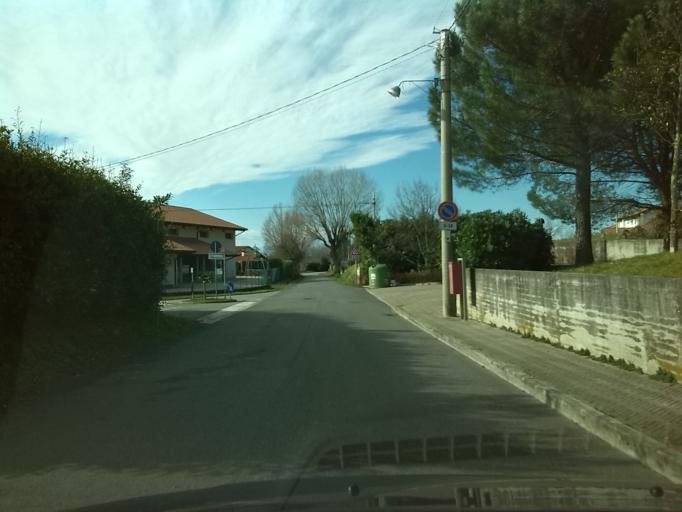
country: IT
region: Friuli Venezia Giulia
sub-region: Provincia di Gorizia
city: Cormons
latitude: 45.9668
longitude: 13.4646
